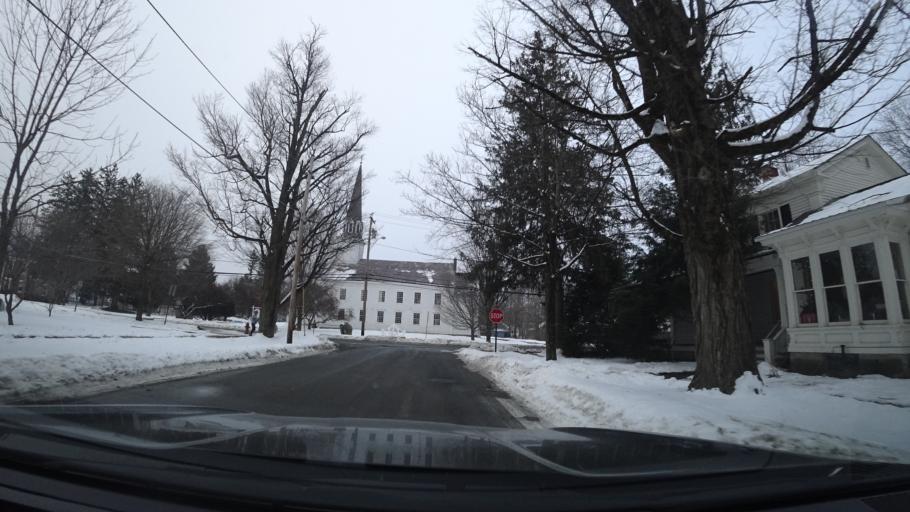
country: US
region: New York
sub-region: Washington County
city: Cambridge
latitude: 43.1723
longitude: -73.3291
